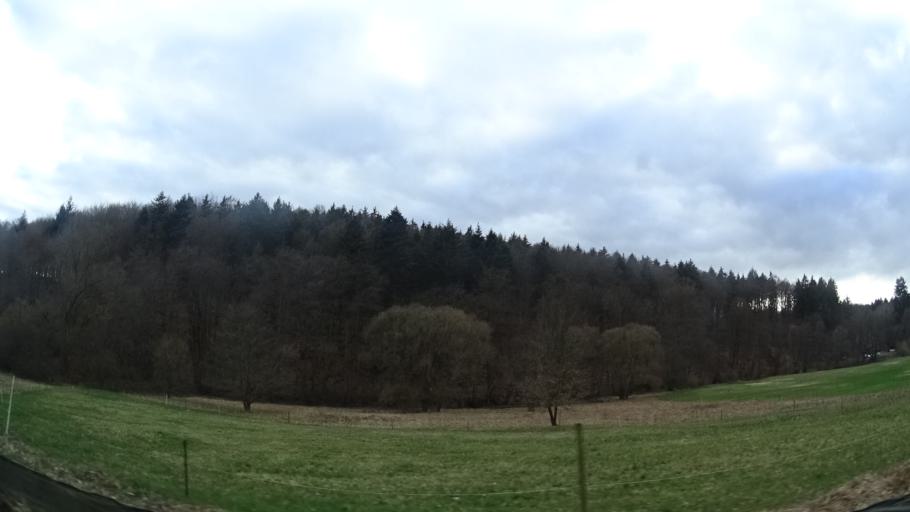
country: DE
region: Hesse
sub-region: Regierungsbezirk Darmstadt
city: Wiesbaden
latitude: 50.1164
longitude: 8.2605
